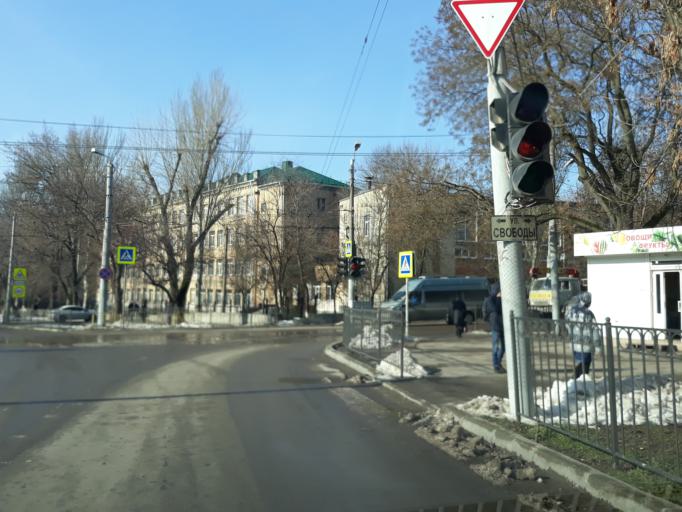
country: RU
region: Rostov
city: Taganrog
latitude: 47.2053
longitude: 38.8943
